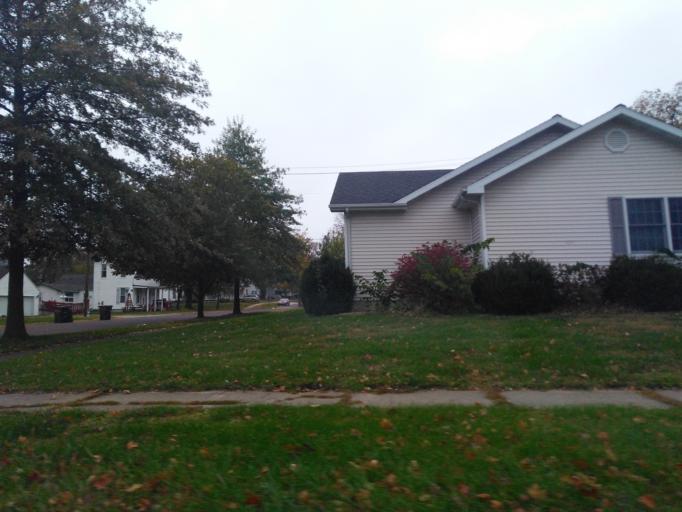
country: US
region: Illinois
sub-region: Bond County
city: Greenville
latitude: 38.8889
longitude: -89.4134
